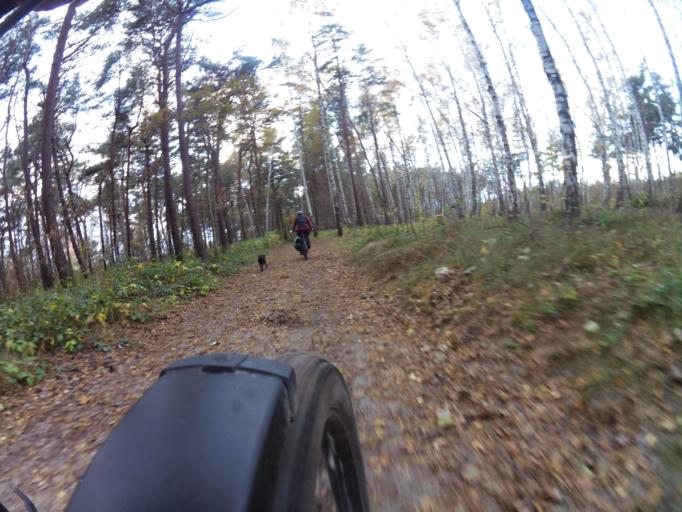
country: PL
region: Pomeranian Voivodeship
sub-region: Powiat pucki
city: Jastarnia
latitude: 54.7202
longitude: 18.6253
